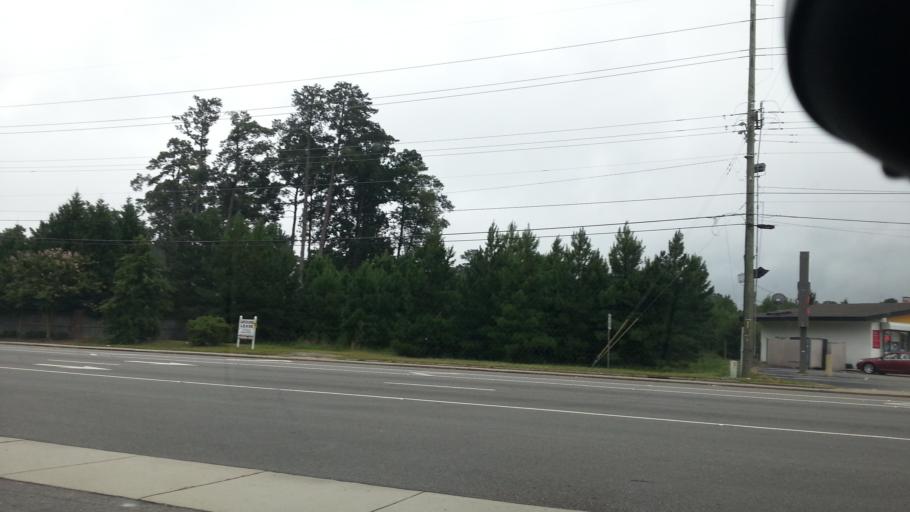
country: US
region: North Carolina
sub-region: Cumberland County
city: Fayetteville
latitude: 35.0673
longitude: -78.9499
